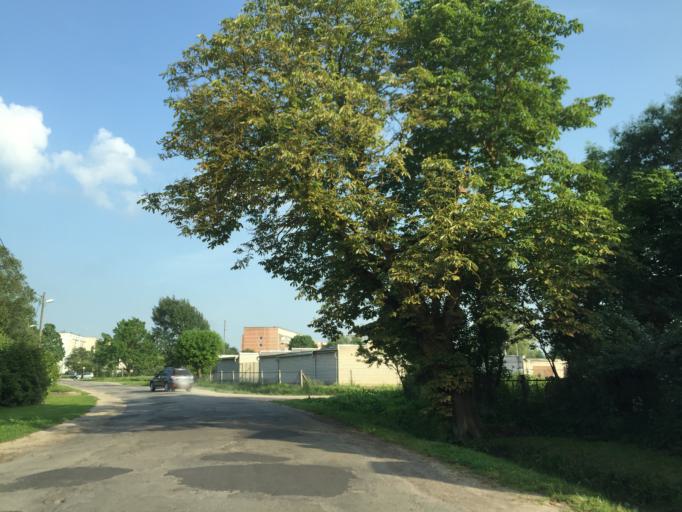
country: LV
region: Jelgava
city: Jelgava
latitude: 56.6635
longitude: 23.7010
